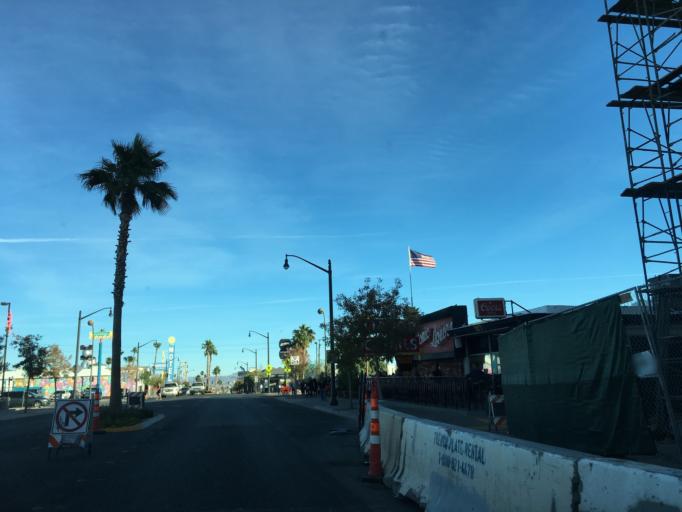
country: US
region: Nevada
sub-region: Clark County
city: Las Vegas
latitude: 36.1671
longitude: -115.1358
